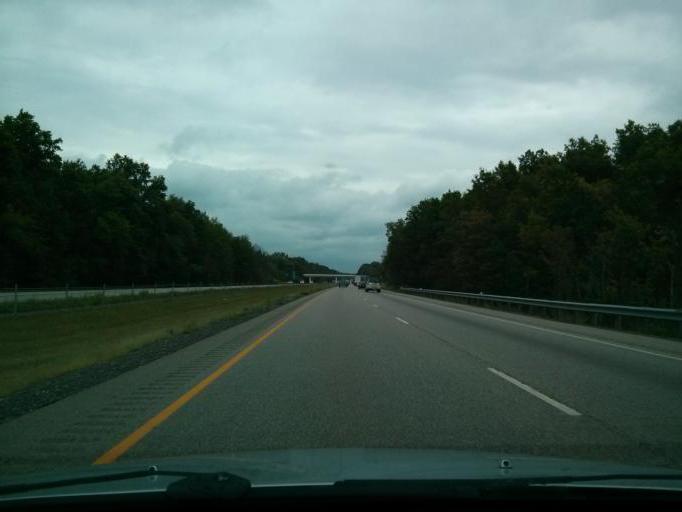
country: US
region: Ohio
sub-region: Portage County
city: Ravenna
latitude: 41.1108
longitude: -81.2758
